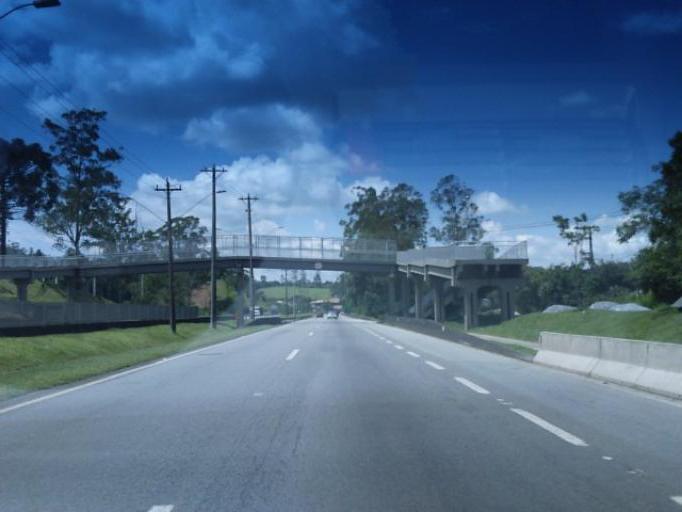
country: BR
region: Sao Paulo
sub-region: Sao Lourenco Da Serra
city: Sao Lourenco da Serra
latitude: -23.8516
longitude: -46.9392
